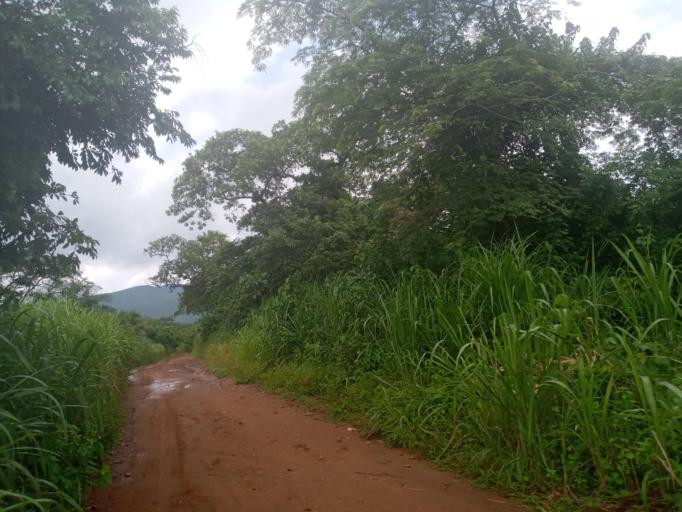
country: SL
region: Northern Province
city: Bumbuna
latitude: 8.9322
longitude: -11.7487
